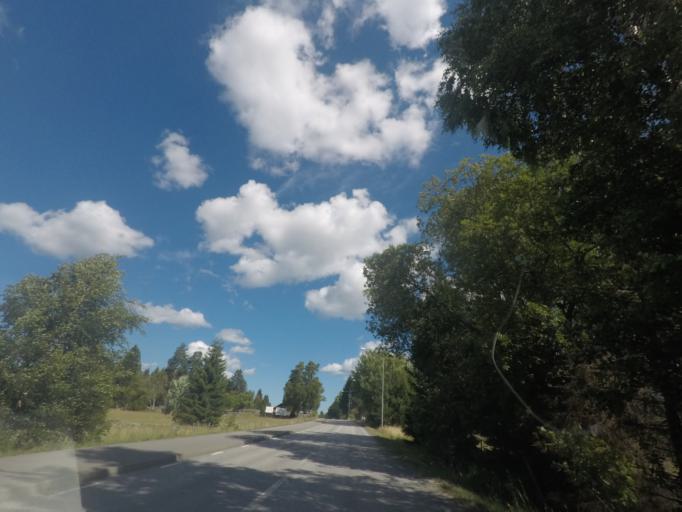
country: SE
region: Stockholm
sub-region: Norrtalje Kommun
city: Hallstavik
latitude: 59.9615
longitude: 18.7989
